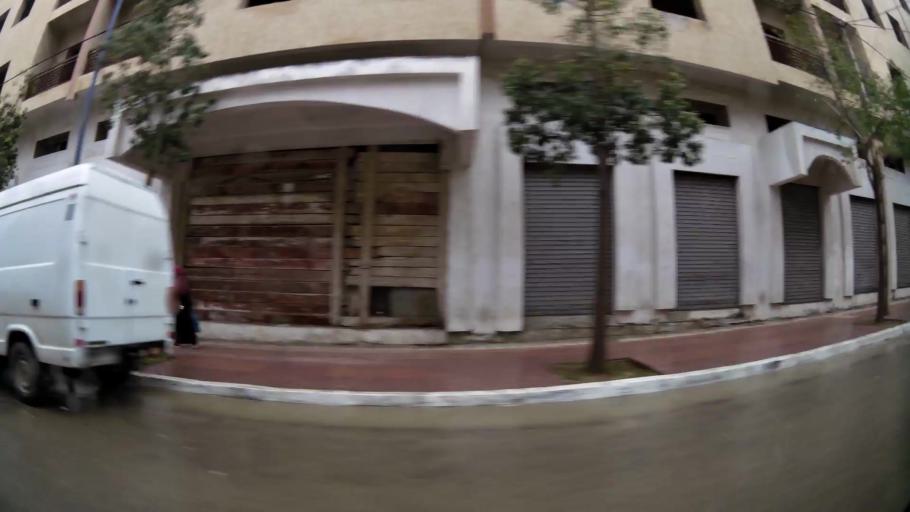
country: MA
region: Taza-Al Hoceima-Taounate
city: Al Hoceima
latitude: 35.2487
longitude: -3.9323
